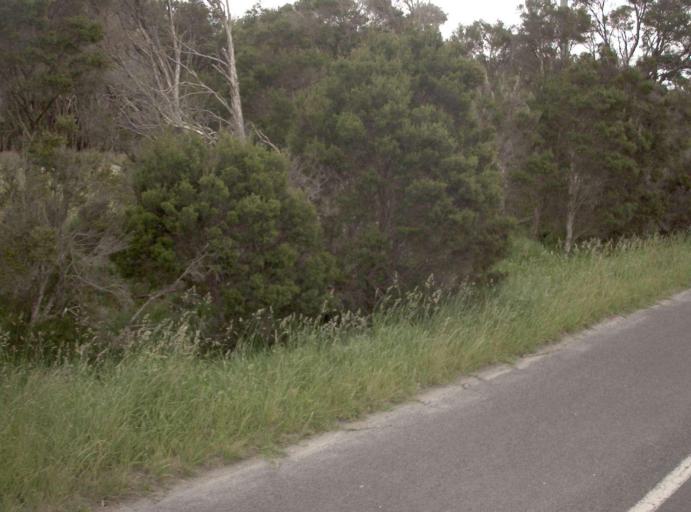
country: AU
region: Victoria
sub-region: Cardinia
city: Koo-Wee-Rup
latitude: -38.2742
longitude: 145.5476
